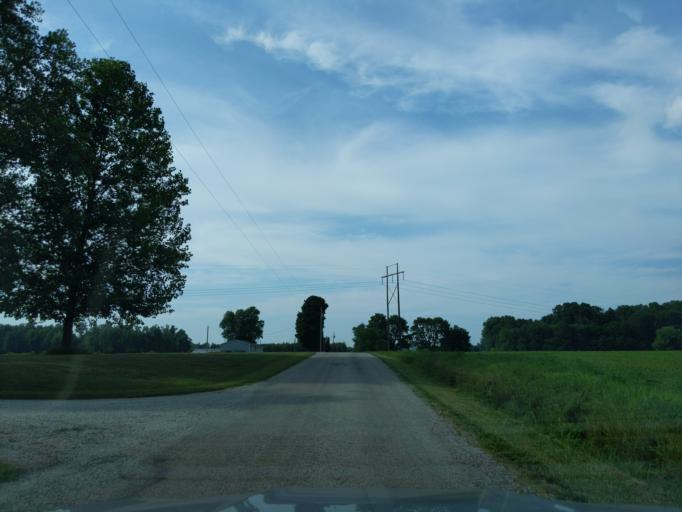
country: US
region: Indiana
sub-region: Ripley County
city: Osgood
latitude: 39.2026
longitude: -85.3892
